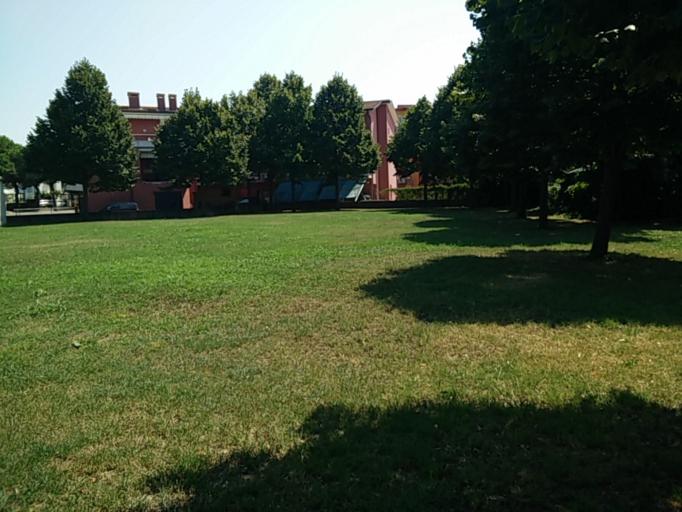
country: IT
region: Veneto
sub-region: Provincia di Venezia
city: Caorle
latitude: 45.6042
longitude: 12.8865
